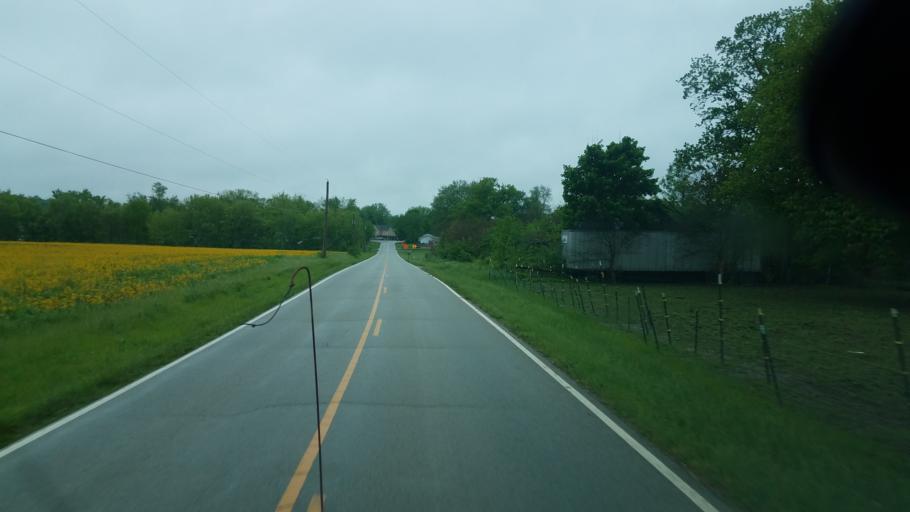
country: US
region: Ohio
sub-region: Highland County
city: Leesburg
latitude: 39.2859
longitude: -83.5873
